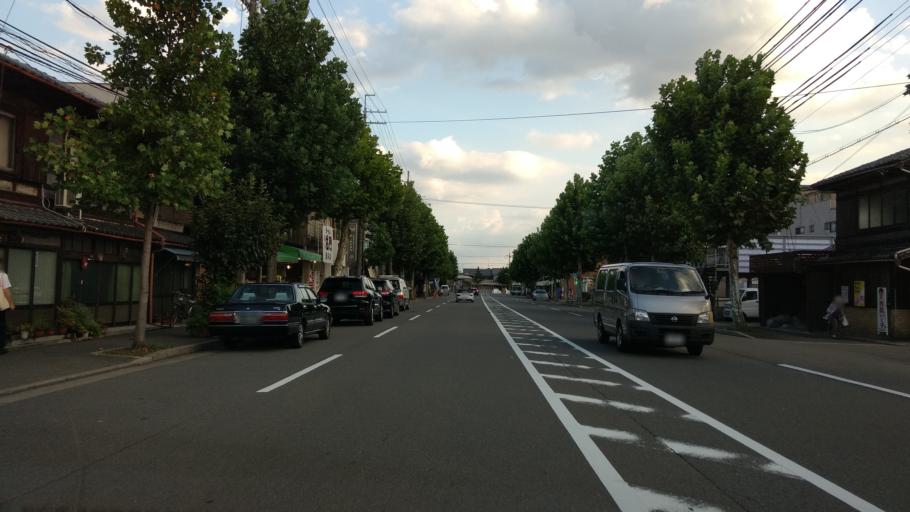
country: JP
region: Kyoto
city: Kyoto
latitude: 34.9912
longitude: 135.7392
